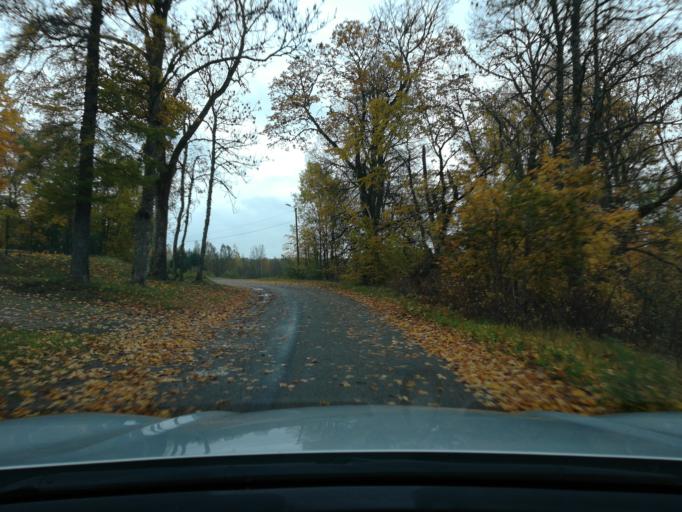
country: EE
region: Ida-Virumaa
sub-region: Johvi vald
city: Johvi
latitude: 59.1907
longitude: 27.5475
